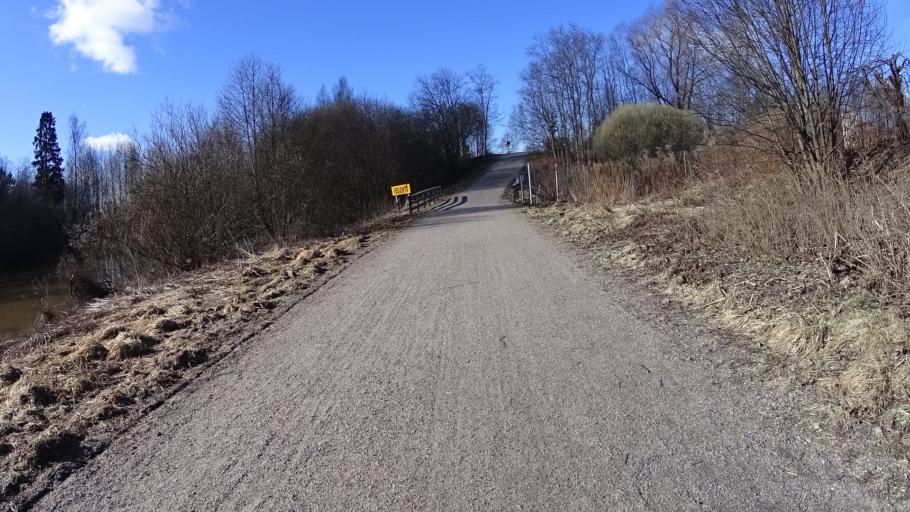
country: FI
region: Uusimaa
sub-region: Helsinki
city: Teekkarikylae
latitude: 60.2733
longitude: 24.8808
